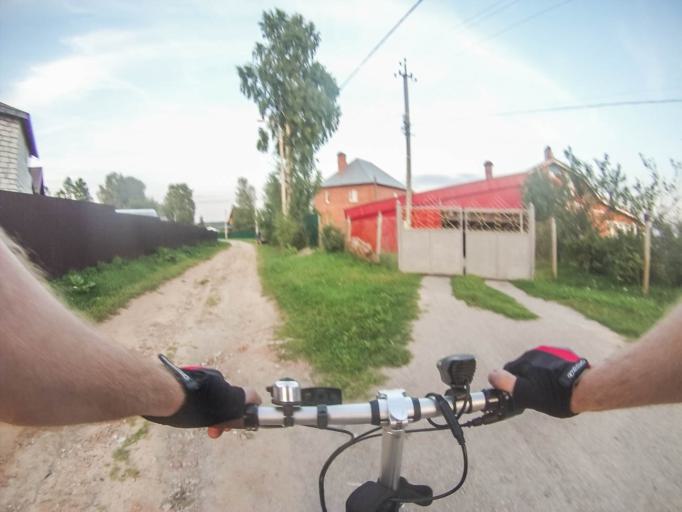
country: RU
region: Jaroslavl
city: Myshkin
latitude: 57.7928
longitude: 38.4710
